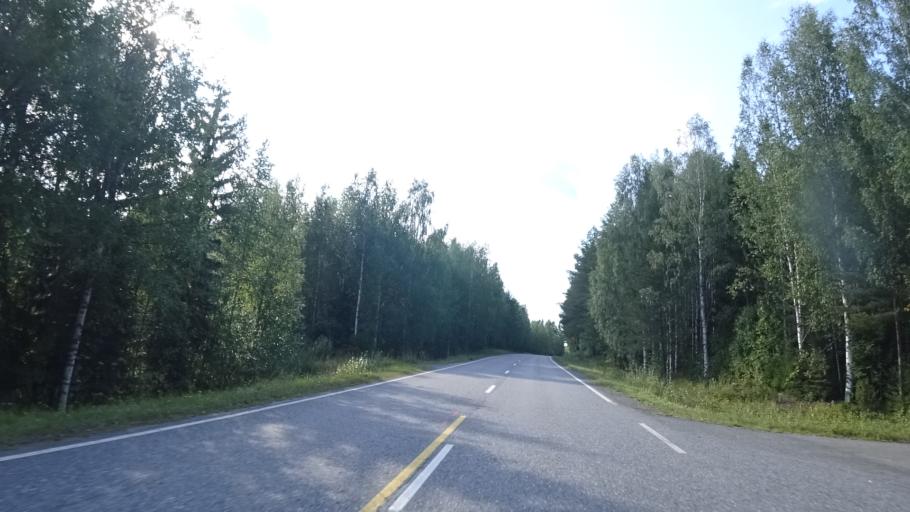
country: FI
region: North Karelia
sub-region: Keski-Karjala
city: Kitee
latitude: 62.0891
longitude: 30.1290
